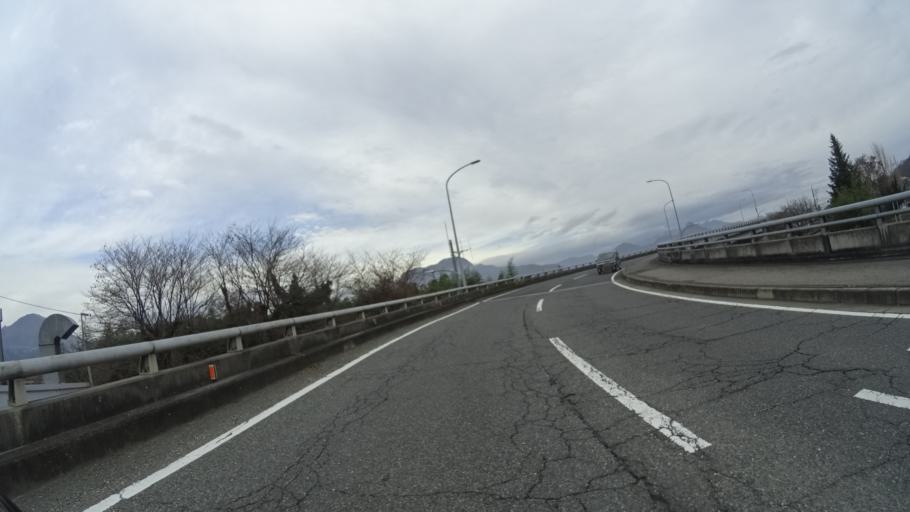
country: JP
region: Gunma
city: Numata
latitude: 36.6468
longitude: 139.0304
